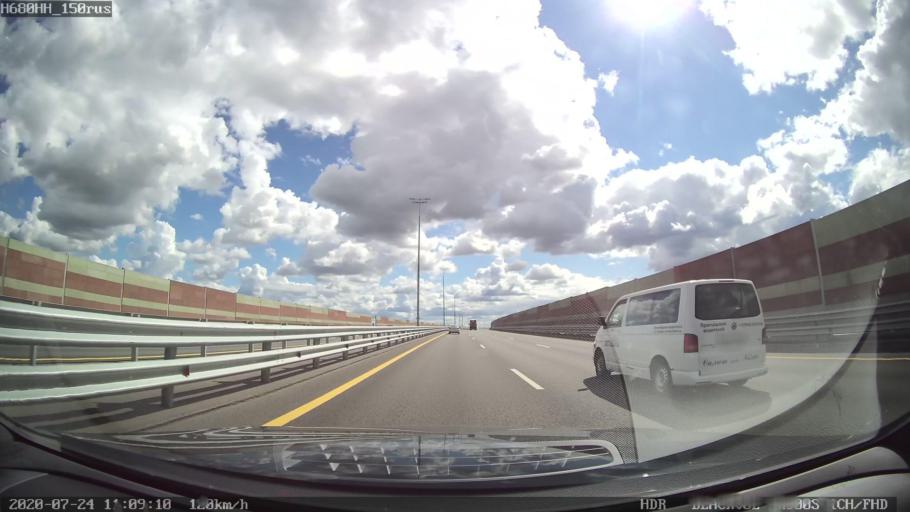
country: RU
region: St.-Petersburg
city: Tyarlevo
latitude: 59.7510
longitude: 30.4647
